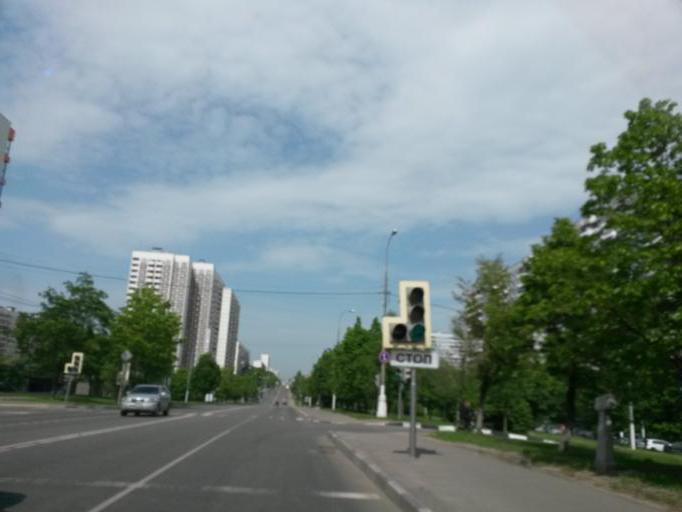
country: RU
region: Moscow
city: Chertanovo Yuzhnoye
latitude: 55.6041
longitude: 37.6001
